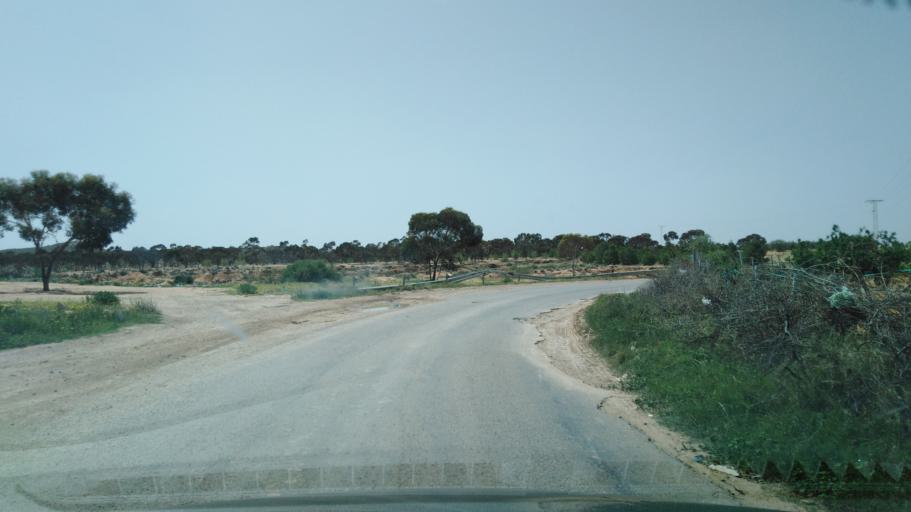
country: TN
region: Safaqis
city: Sfax
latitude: 34.7177
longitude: 10.5319
